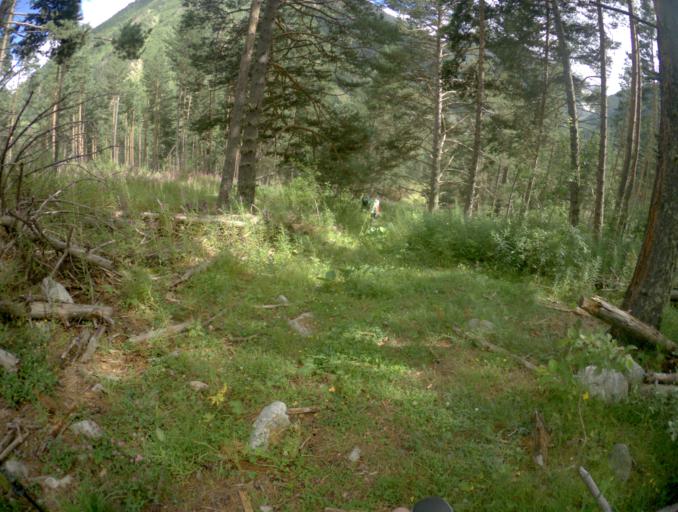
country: RU
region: Karachayevo-Cherkesiya
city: Uchkulan
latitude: 43.3487
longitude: 42.1526
